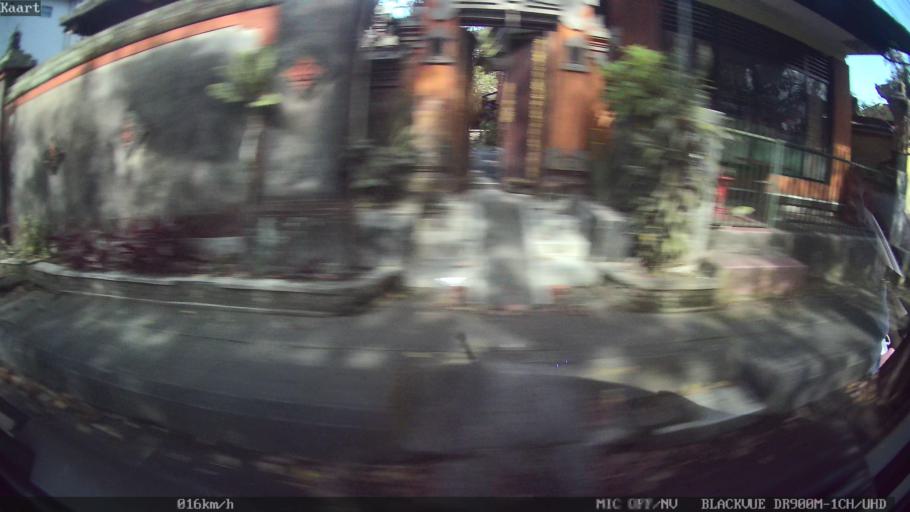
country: ID
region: Bali
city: Tabanan
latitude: -8.5445
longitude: 115.1248
